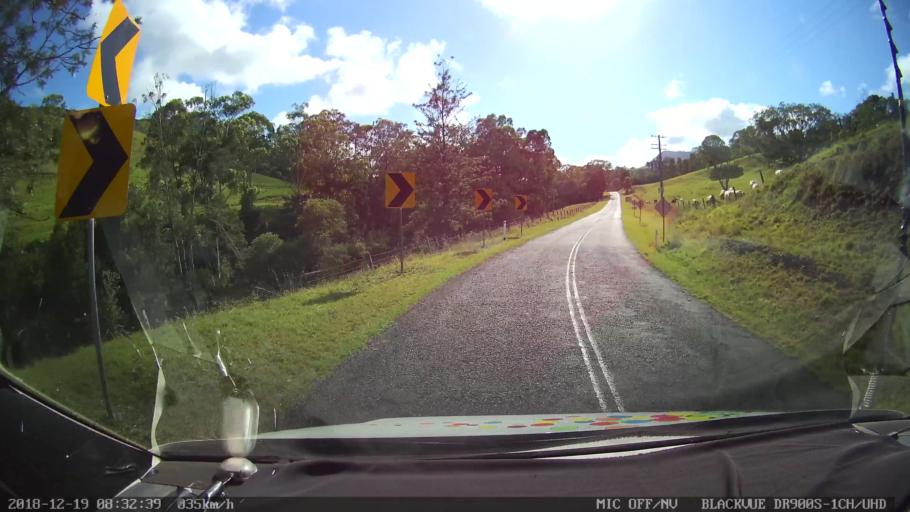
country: AU
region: New South Wales
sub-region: Kyogle
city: Kyogle
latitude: -28.3204
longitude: 152.9425
